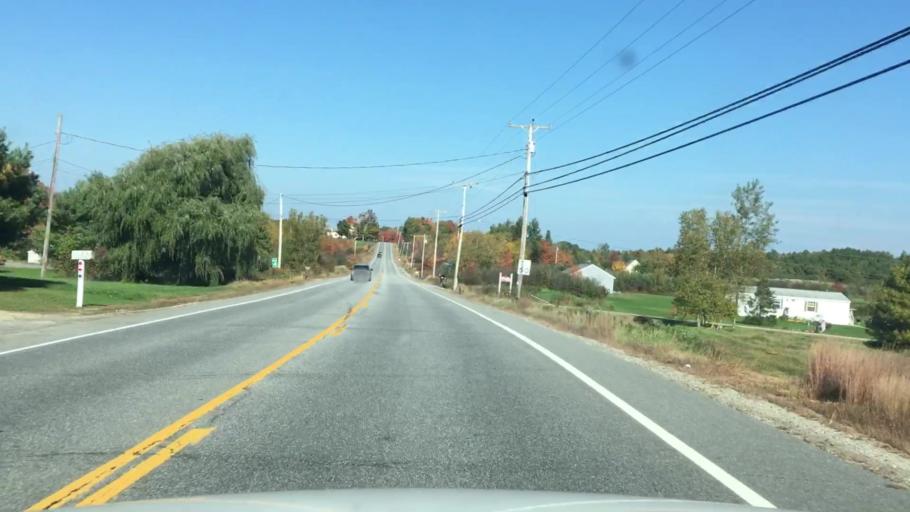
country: US
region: Maine
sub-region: Sagadahoc County
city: Topsham
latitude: 43.9722
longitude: -69.9578
